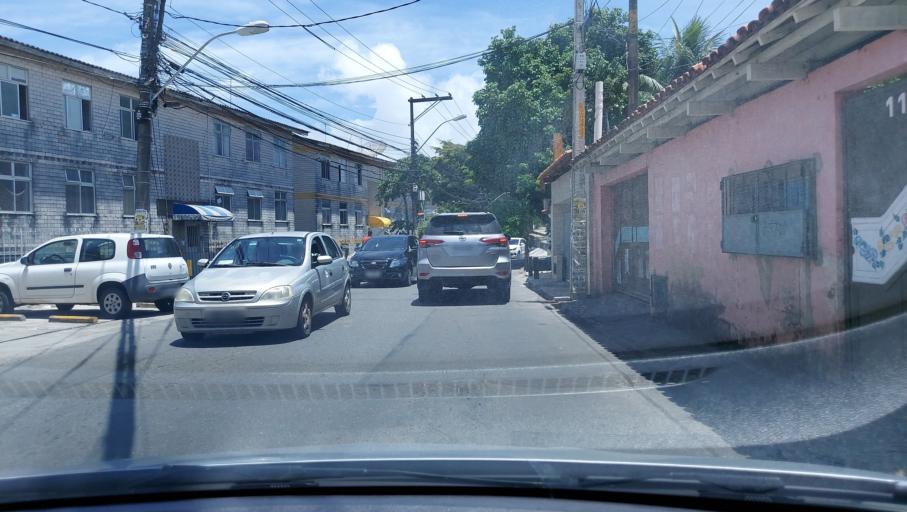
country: BR
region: Bahia
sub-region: Salvador
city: Salvador
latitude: -12.9862
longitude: -38.4752
